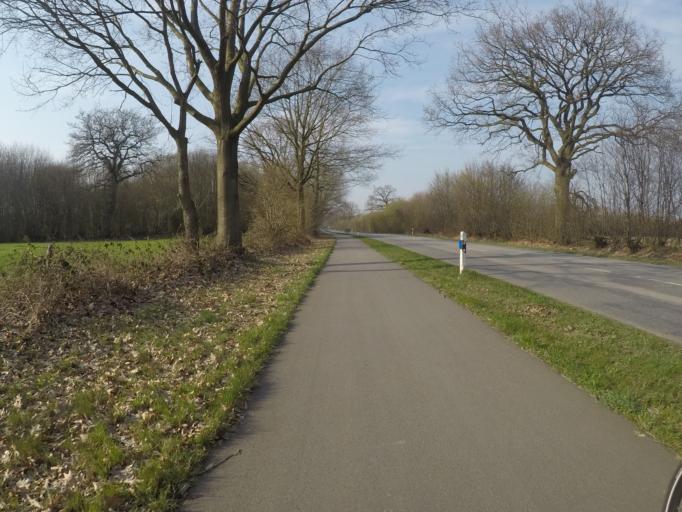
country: DE
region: Schleswig-Holstein
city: Wittenborn
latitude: 53.9393
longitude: 10.2234
